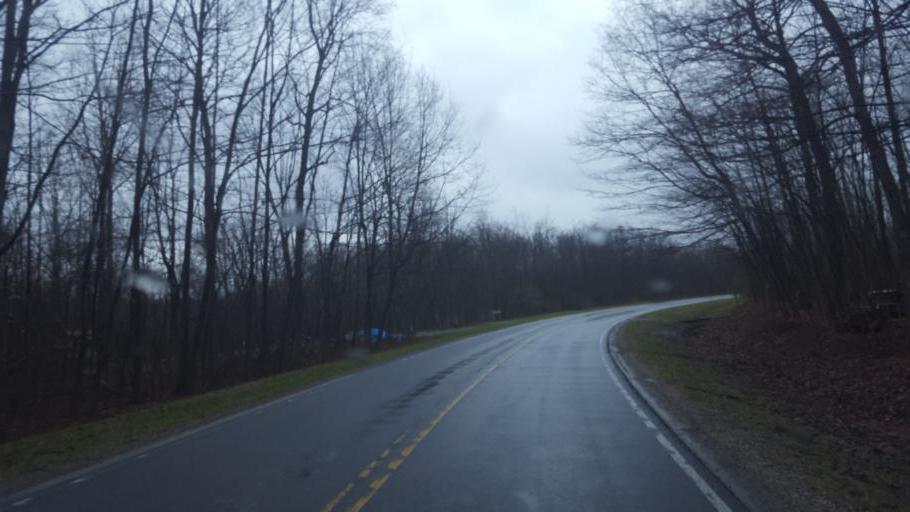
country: US
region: Ohio
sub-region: Delaware County
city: Lewis Center
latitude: 40.1987
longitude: -82.9387
